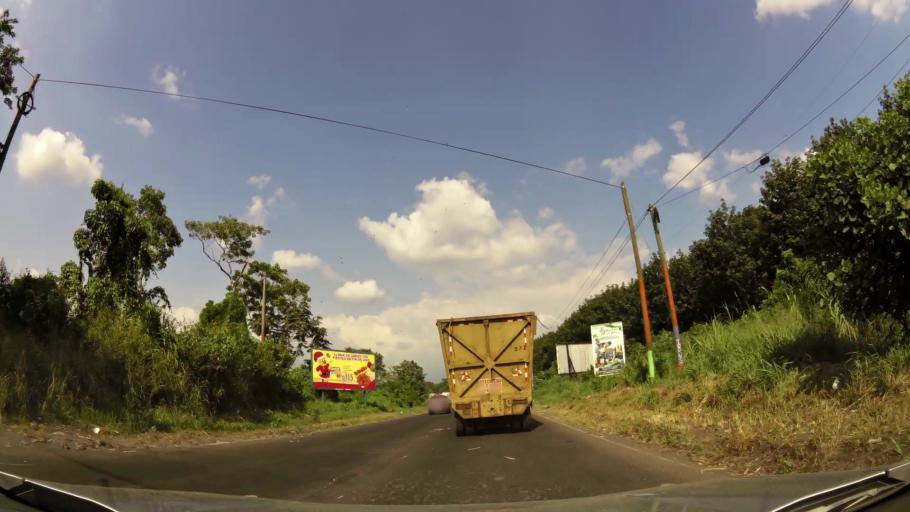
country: GT
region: Retalhuleu
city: San Sebastian
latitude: 14.5554
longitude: -91.6394
